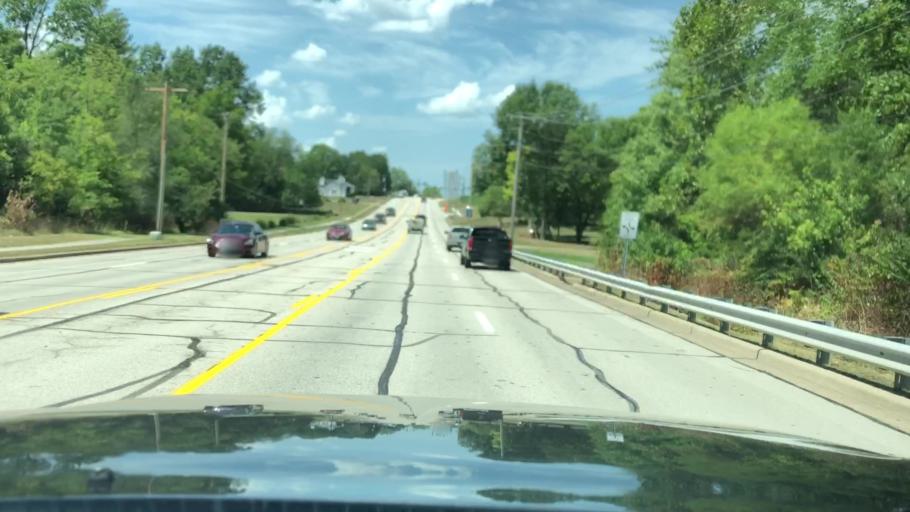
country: US
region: Missouri
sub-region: Saint Charles County
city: O'Fallon
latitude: 38.7914
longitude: -90.6864
